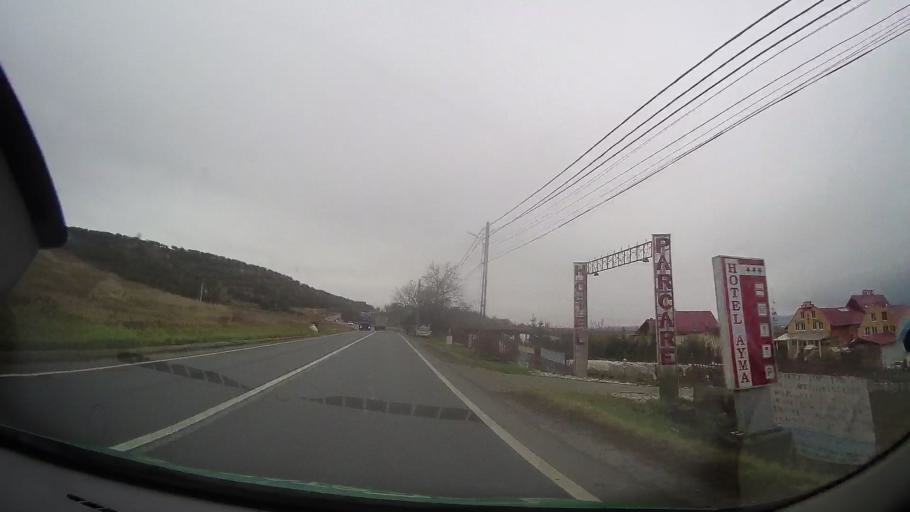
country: RO
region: Mures
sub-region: Comuna Breaza
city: Breaza
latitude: 46.7699
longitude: 24.6577
